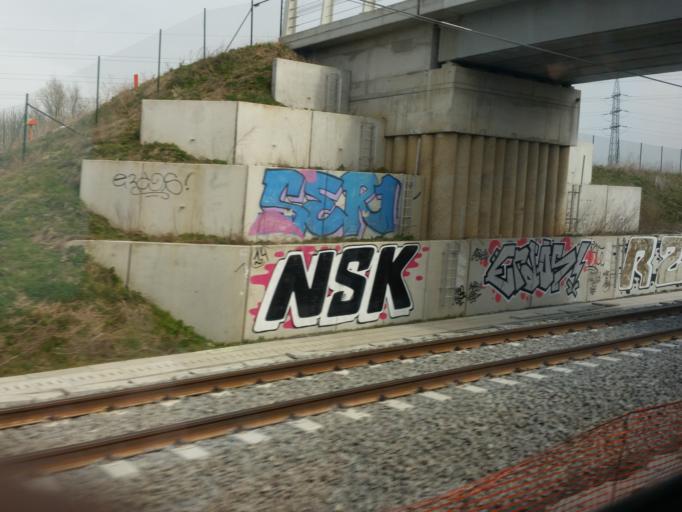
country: BE
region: Flanders
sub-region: Provincie Vlaams-Brabant
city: Dilbeek
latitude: 50.8200
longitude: 4.2604
